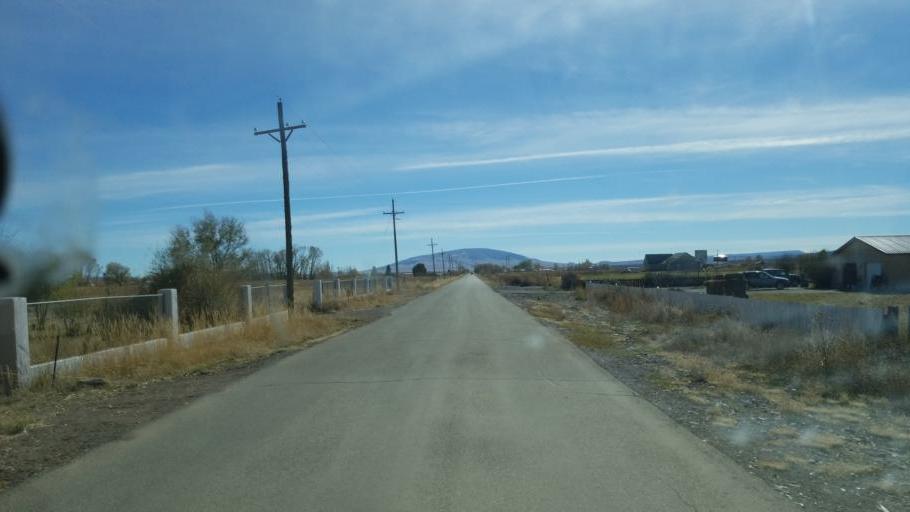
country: US
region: Colorado
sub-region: Conejos County
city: Conejos
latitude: 37.0860
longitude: -106.0194
